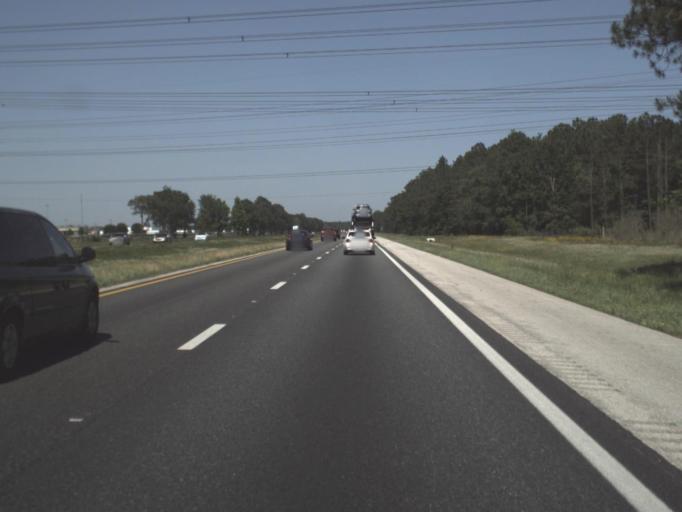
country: US
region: Florida
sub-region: Duval County
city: Baldwin
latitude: 30.2930
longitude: -81.9515
